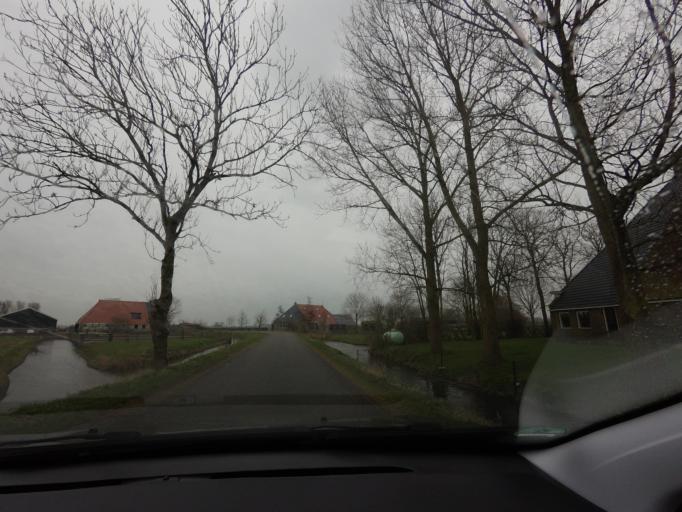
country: NL
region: Friesland
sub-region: Sudwest Fryslan
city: Bolsward
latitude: 53.0772
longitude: 5.5549
